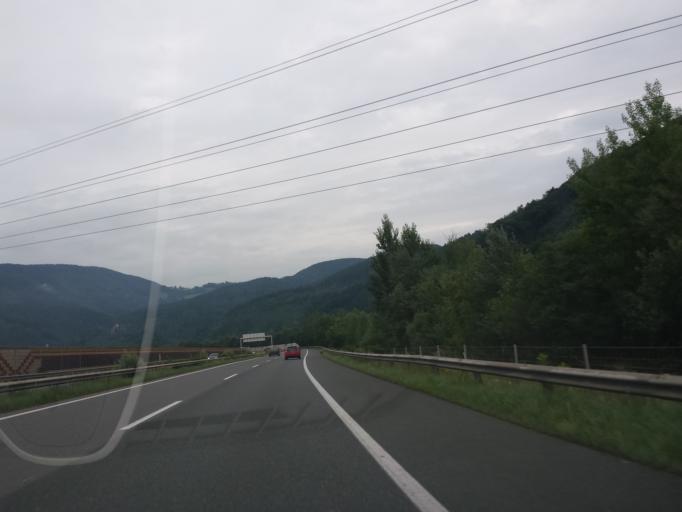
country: AT
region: Styria
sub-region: Politischer Bezirk Graz-Umgebung
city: Deutschfeistritz
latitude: 47.1899
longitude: 15.3382
